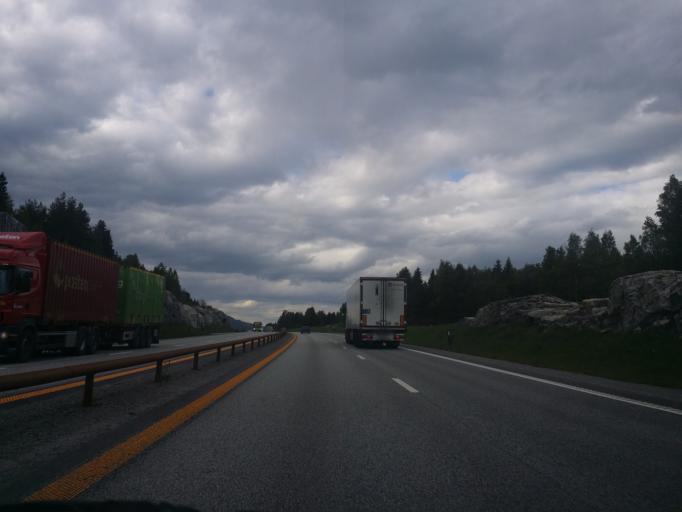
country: NO
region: Akershus
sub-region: Eidsvoll
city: Raholt
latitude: 60.2943
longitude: 11.1362
